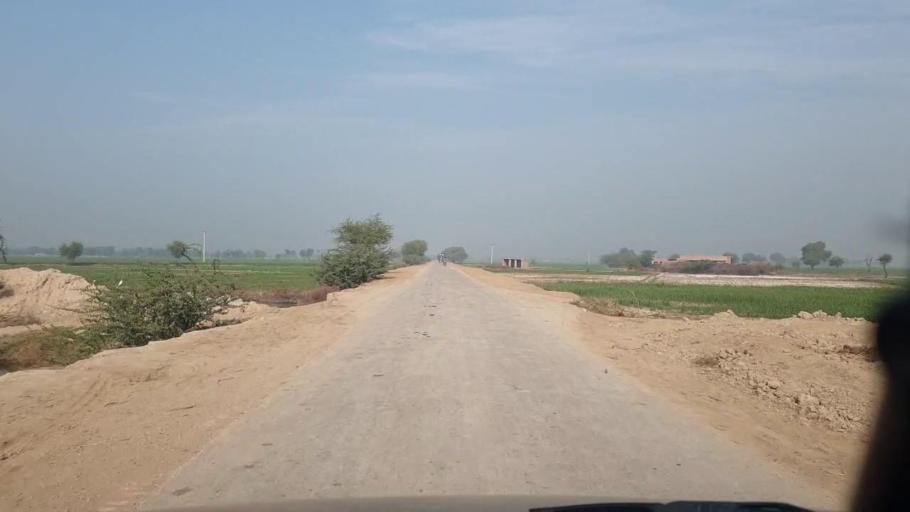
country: PK
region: Sindh
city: Shahdadpur
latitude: 25.9932
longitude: 68.5623
